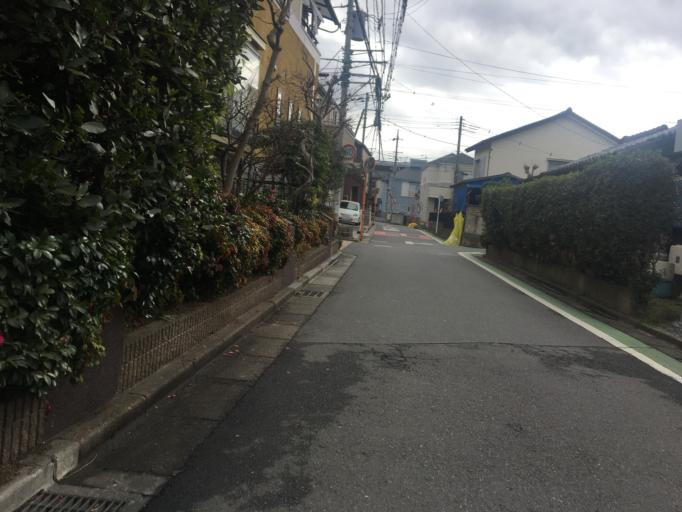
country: JP
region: Saitama
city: Shiki
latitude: 35.8314
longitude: 139.5825
